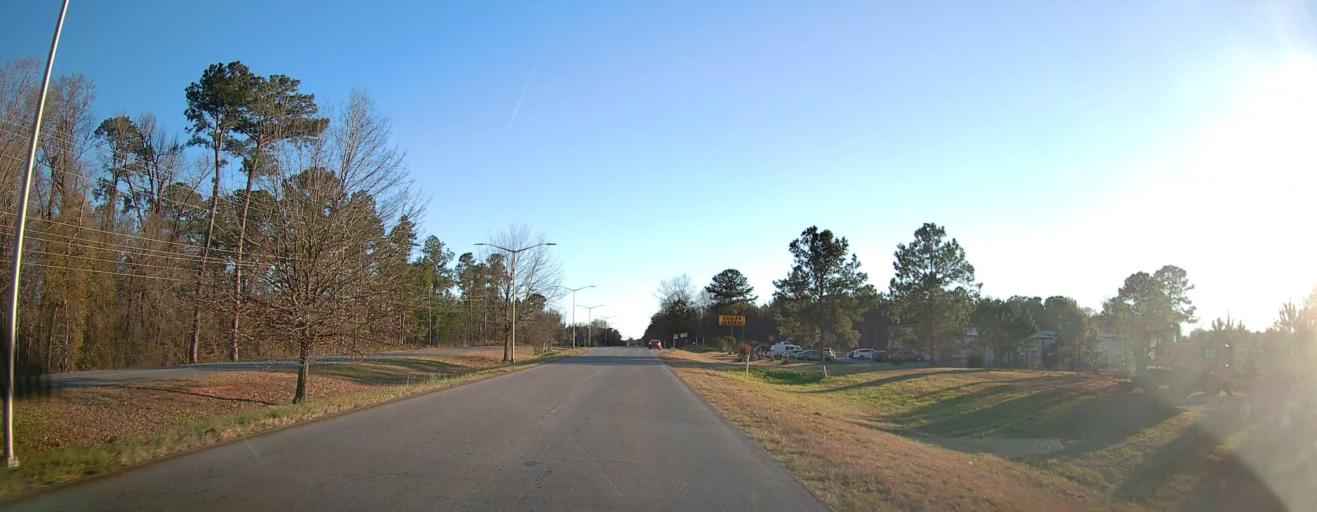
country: US
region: Georgia
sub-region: Dougherty County
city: Albany
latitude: 31.5745
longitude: -84.2206
